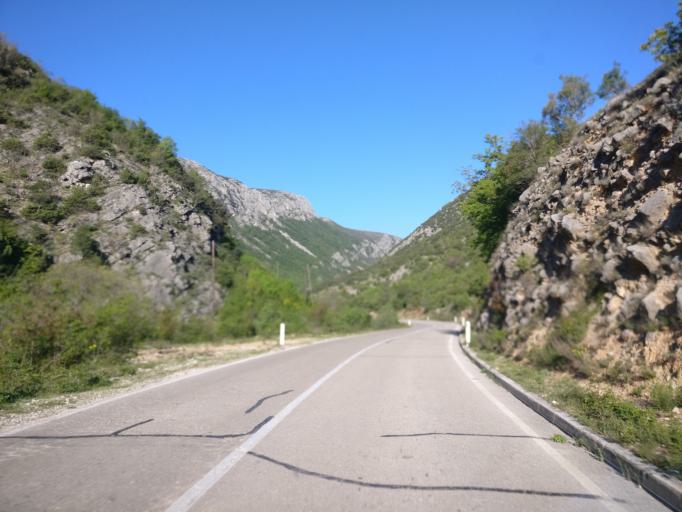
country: BA
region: Federation of Bosnia and Herzegovina
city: Stolac
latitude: 43.0720
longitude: 18.0455
